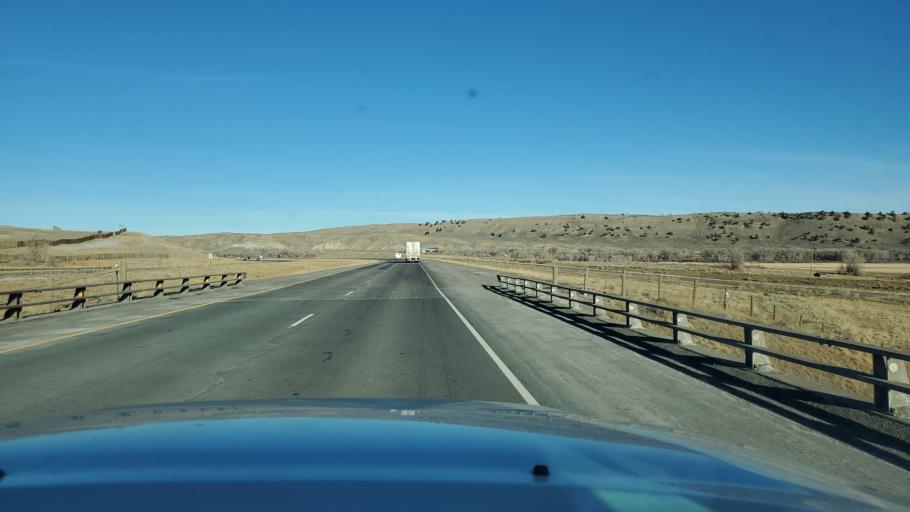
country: US
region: Wyoming
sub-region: Carbon County
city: Saratoga
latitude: 41.6926
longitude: -106.3833
